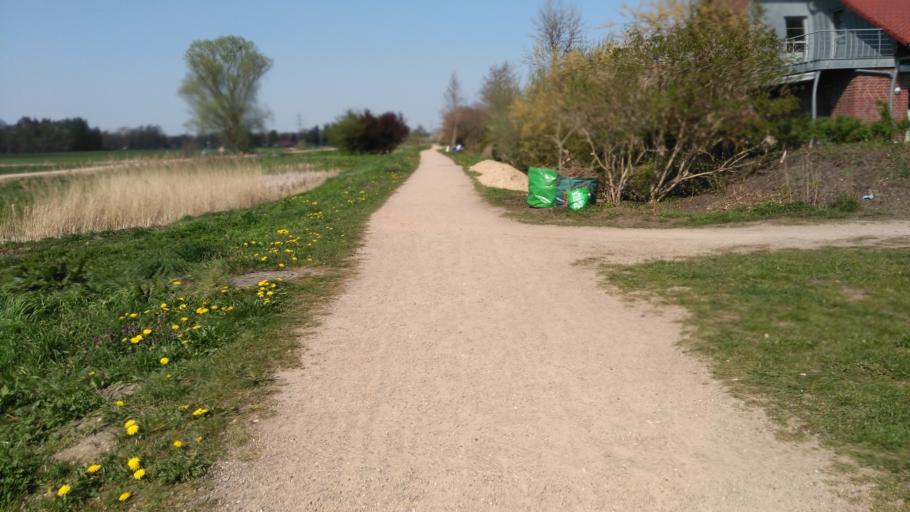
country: DE
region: Lower Saxony
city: Buxtehude
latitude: 53.4782
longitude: 9.6820
